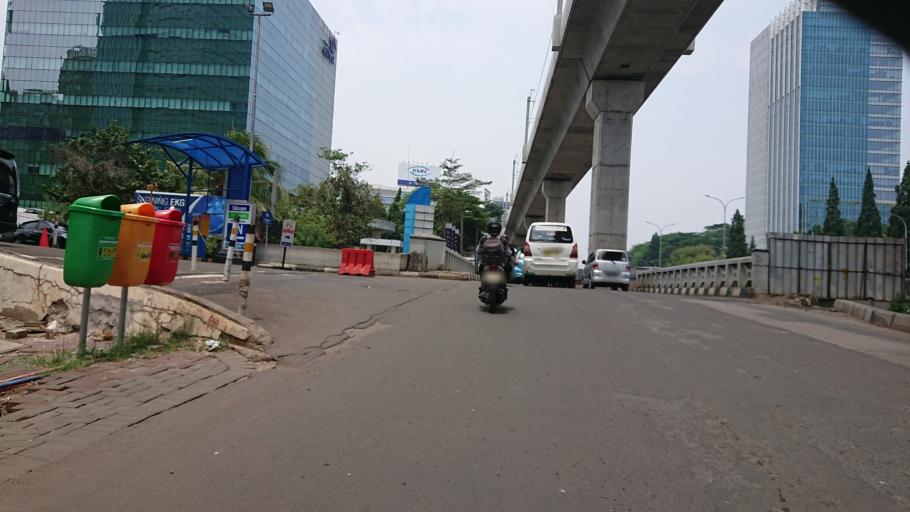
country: ID
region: Banten
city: South Tangerang
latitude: -6.2920
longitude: 106.7845
